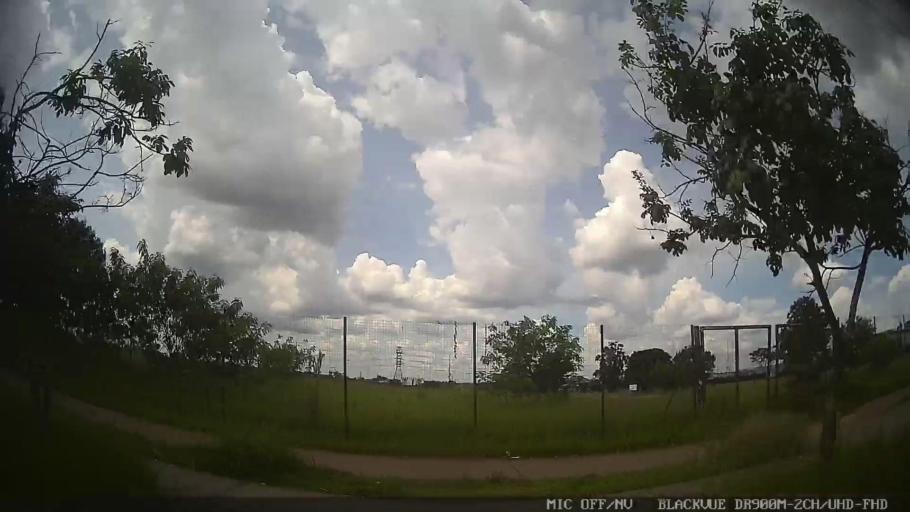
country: BR
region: Sao Paulo
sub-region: Suzano
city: Suzano
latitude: -23.5350
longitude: -46.3267
